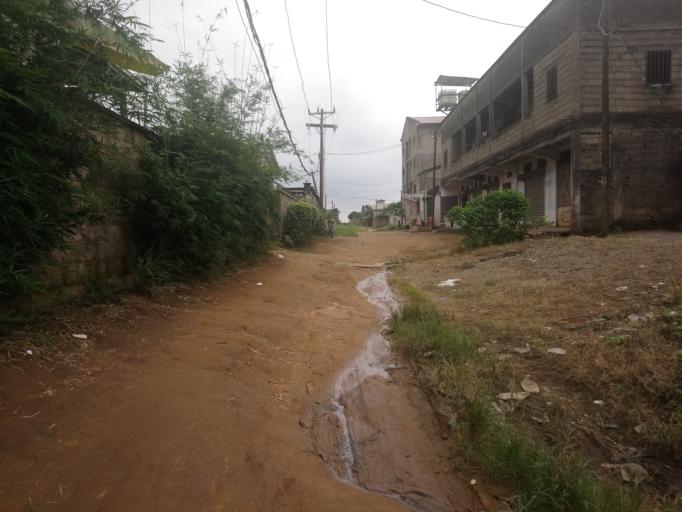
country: CM
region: Littoral
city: Douala
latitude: 4.0937
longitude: 9.7640
